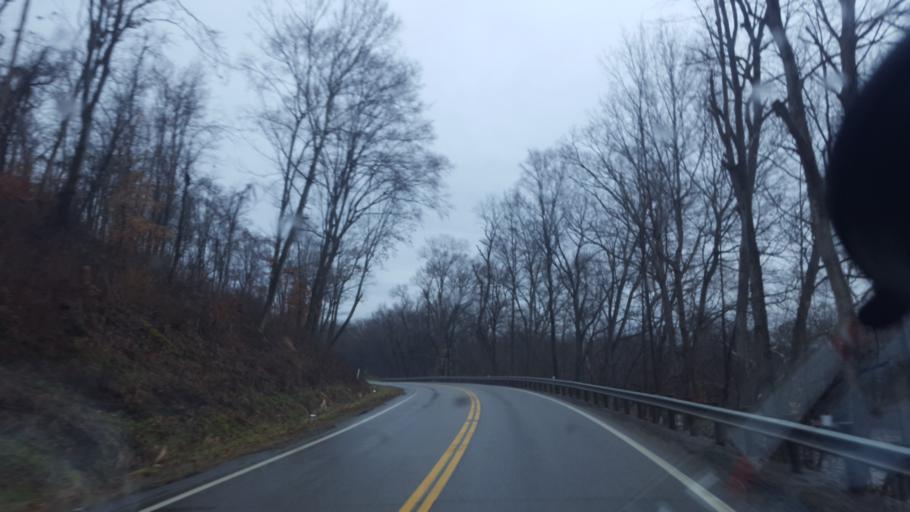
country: US
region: Ohio
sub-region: Tuscarawas County
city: Newcomerstown
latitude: 40.2729
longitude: -81.5484
